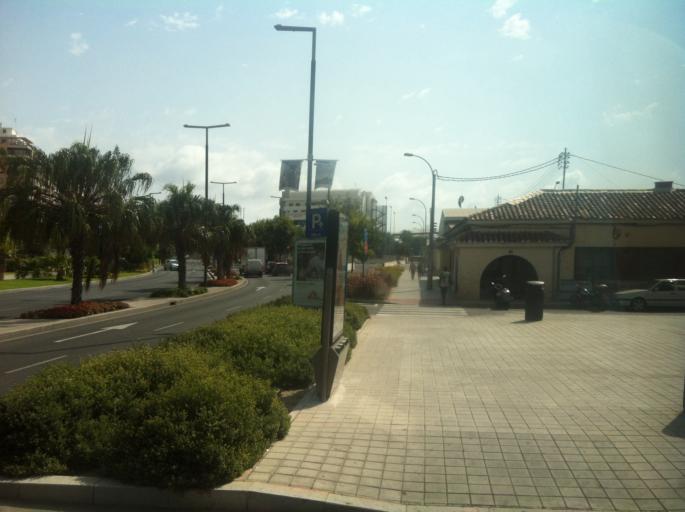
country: ES
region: Valencia
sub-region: Provincia de Alicante
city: Alicante
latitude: 38.3379
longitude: -0.4914
